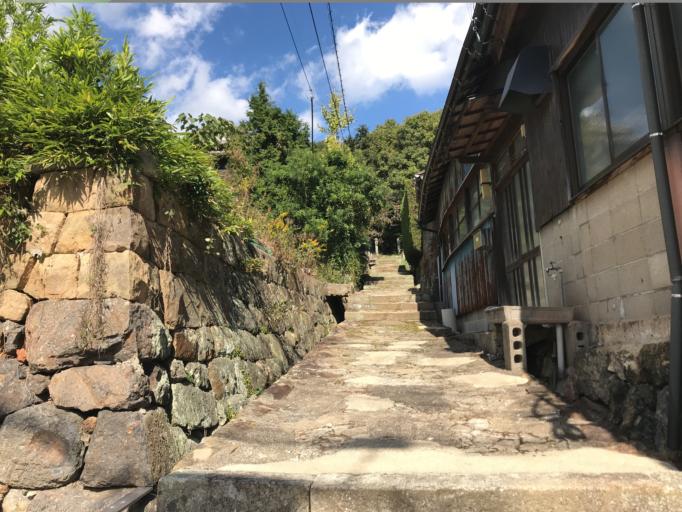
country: JP
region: Saga Prefecture
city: Imaricho-ko
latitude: 33.1904
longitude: 129.8959
